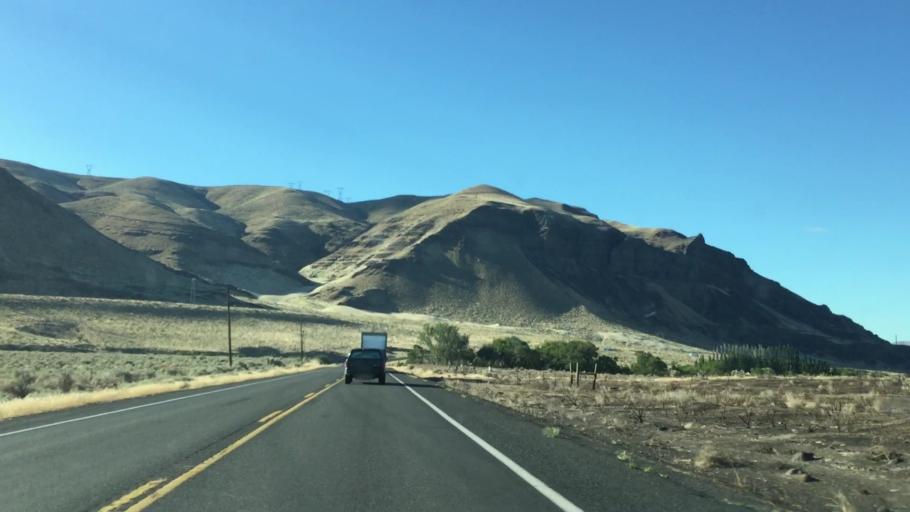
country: US
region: Washington
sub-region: Grant County
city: Mattawa
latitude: 46.8196
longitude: -119.9241
